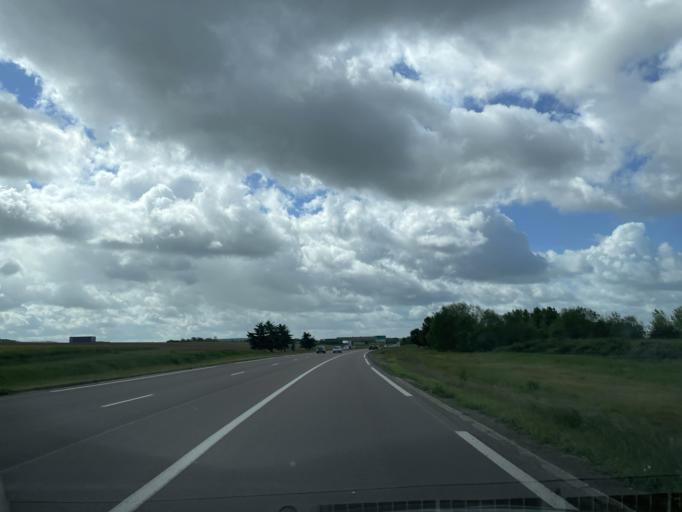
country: FR
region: Bourgogne
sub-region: Departement de l'Yonne
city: Saint-Clement
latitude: 48.2117
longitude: 3.3099
